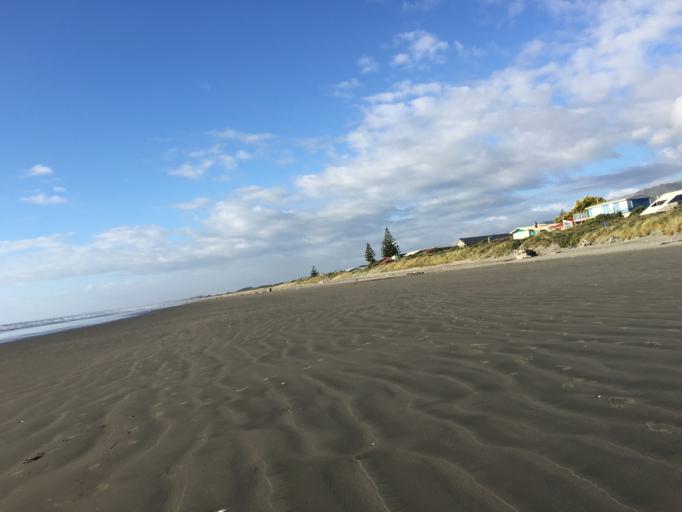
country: NZ
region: Wellington
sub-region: Kapiti Coast District
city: Paraparaumu
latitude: -40.8545
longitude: 175.0310
